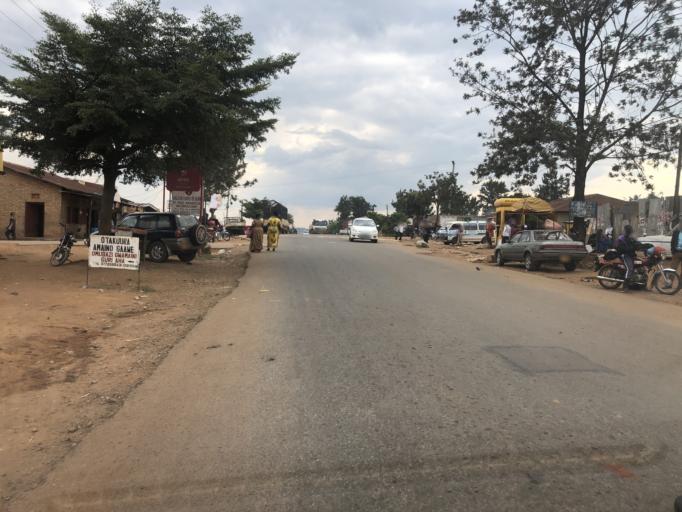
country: UG
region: Western Region
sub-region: Sheema District
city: Kibingo
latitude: -0.5789
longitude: 30.4079
